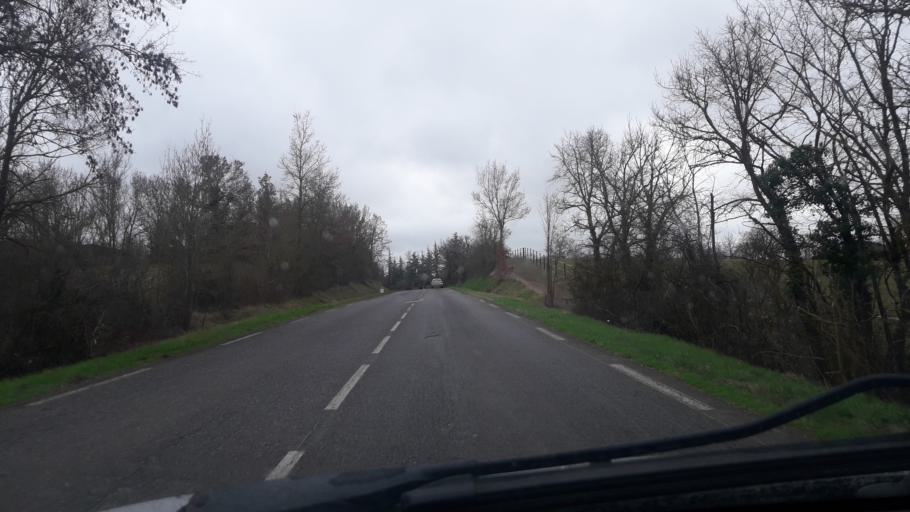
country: FR
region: Midi-Pyrenees
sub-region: Departement du Gers
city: Gimont
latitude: 43.6961
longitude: 0.9975
